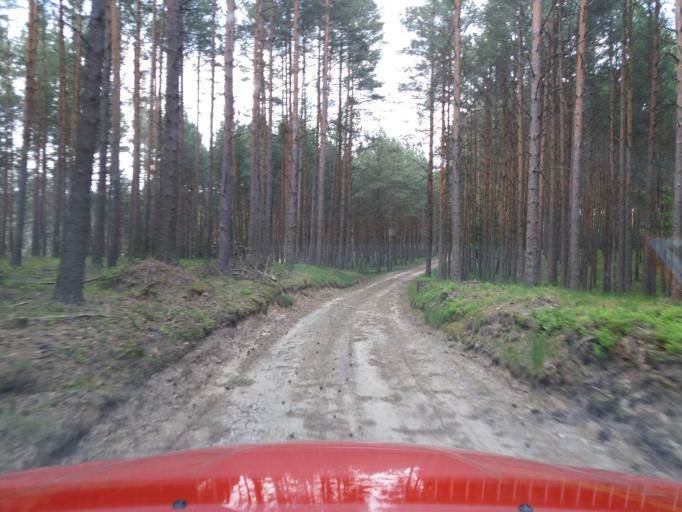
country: PL
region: West Pomeranian Voivodeship
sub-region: Powiat choszczenski
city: Drawno
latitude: 53.1381
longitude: 15.7664
